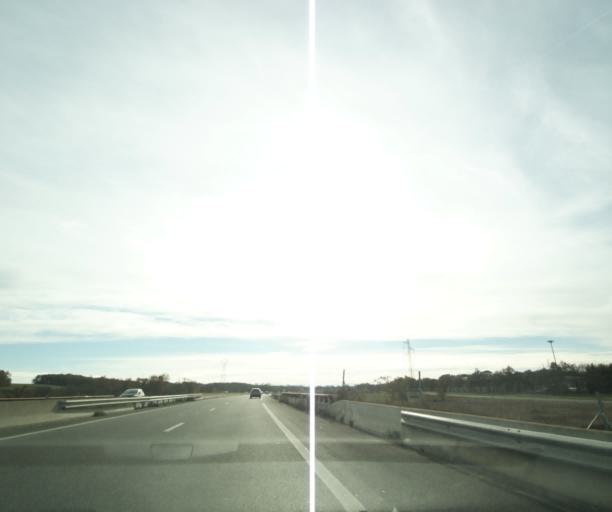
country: FR
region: Midi-Pyrenees
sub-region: Departement de la Haute-Garonne
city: La Salvetat-Saint-Gilles
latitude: 43.5960
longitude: 1.2777
